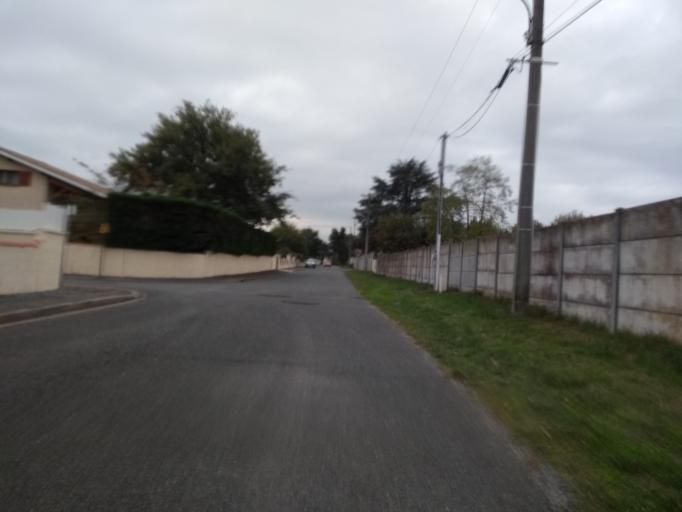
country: FR
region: Aquitaine
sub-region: Departement de la Gironde
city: Talence
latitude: 44.7830
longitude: -0.5899
